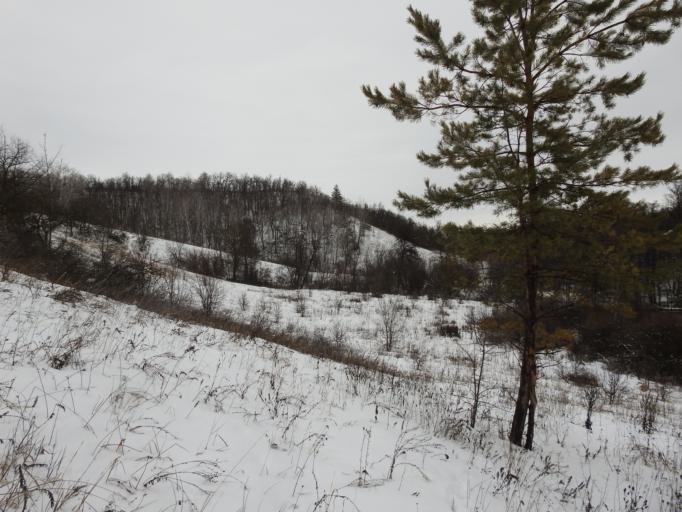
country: RU
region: Saratov
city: Tersa
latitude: 52.1090
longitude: 47.4704
